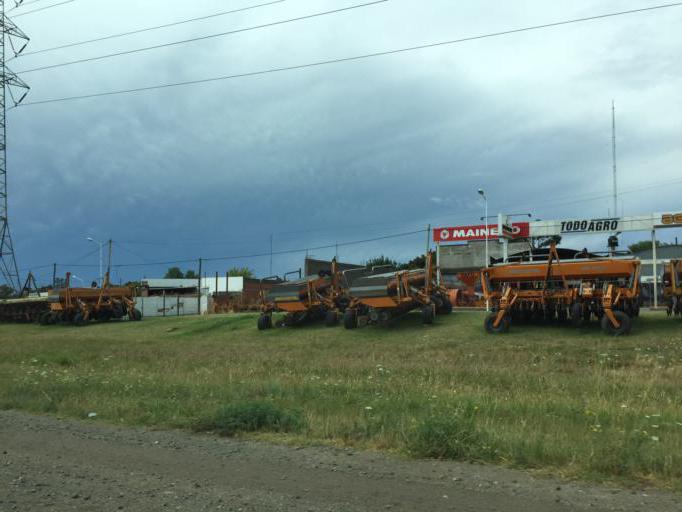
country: AR
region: Buenos Aires
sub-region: Partido de Tandil
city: Tandil
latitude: -37.3142
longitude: -59.1107
